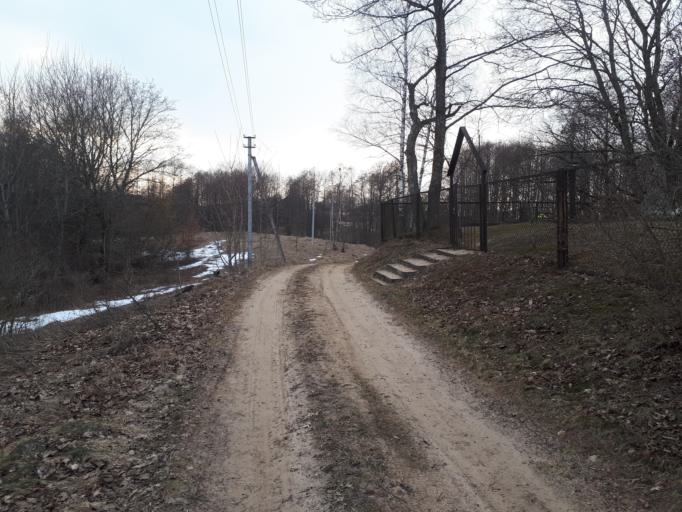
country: LT
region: Alytaus apskritis
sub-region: Alytaus rajonas
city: Daugai
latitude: 54.4278
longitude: 24.2014
